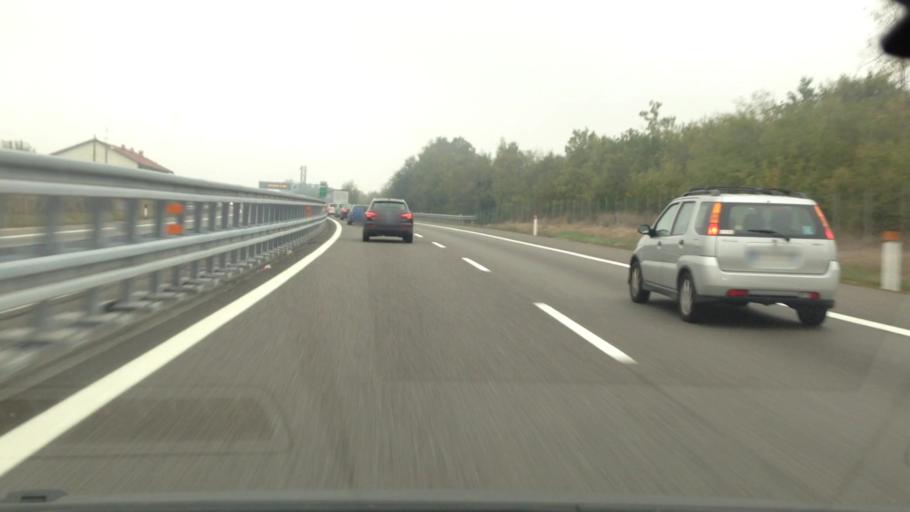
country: IT
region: Piedmont
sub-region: Provincia di Asti
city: Refrancore
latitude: 44.9100
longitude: 8.3269
